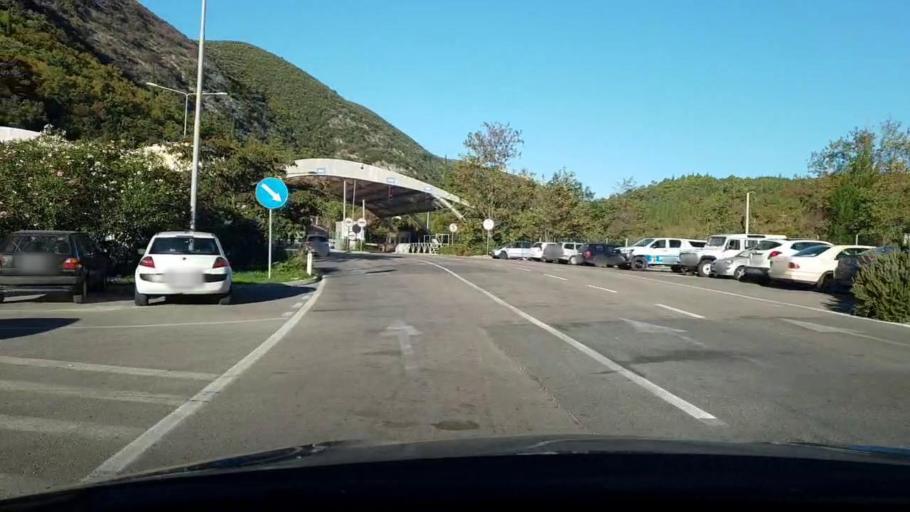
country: ME
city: Igalo
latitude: 42.4811
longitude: 18.4568
